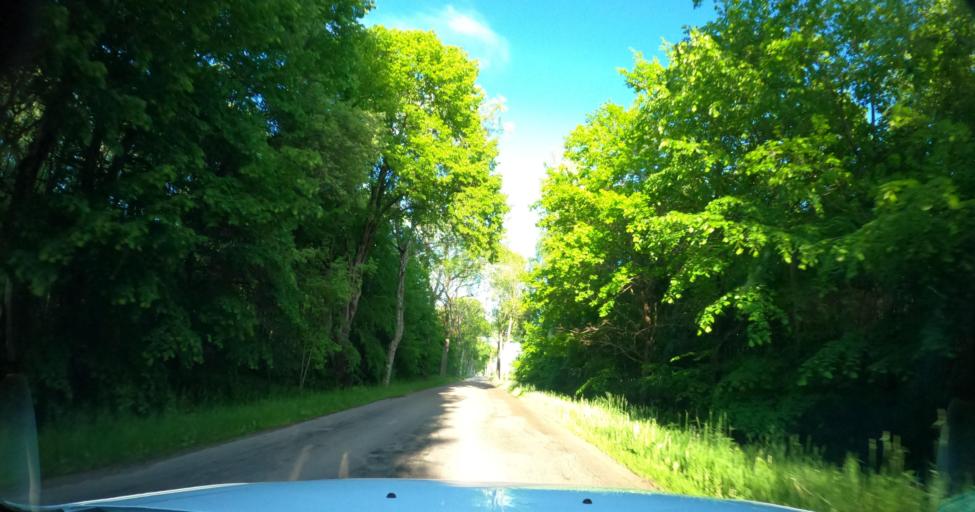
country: PL
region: Warmian-Masurian Voivodeship
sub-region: Powiat braniewski
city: Braniewo
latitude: 54.2811
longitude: 19.8988
